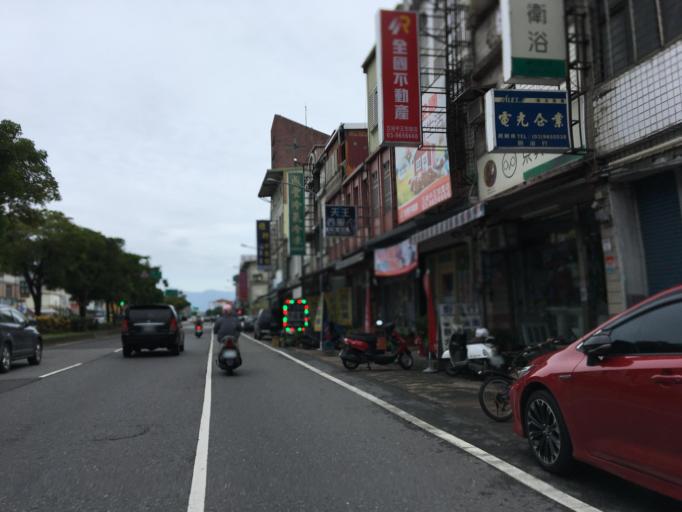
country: TW
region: Taiwan
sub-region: Yilan
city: Yilan
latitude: 24.6960
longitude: 121.7694
